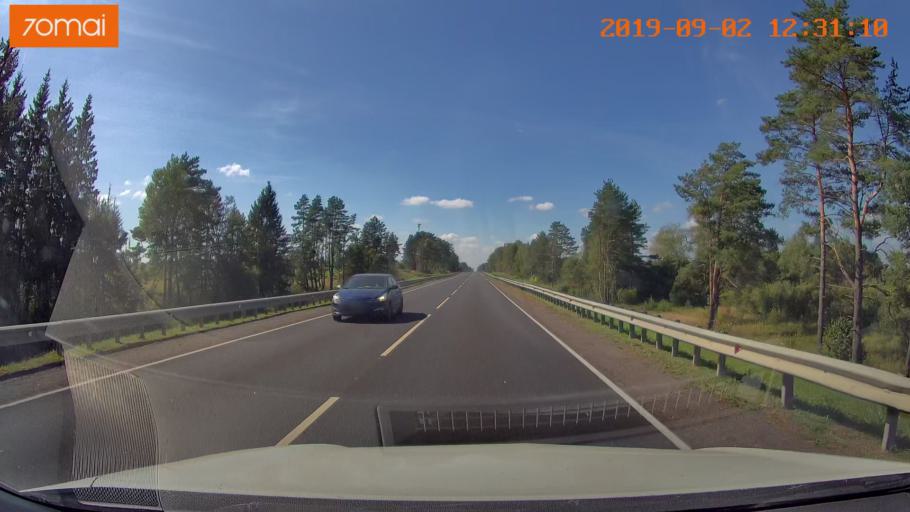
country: RU
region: Smolensk
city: Shumyachi
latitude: 53.8265
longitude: 32.4565
